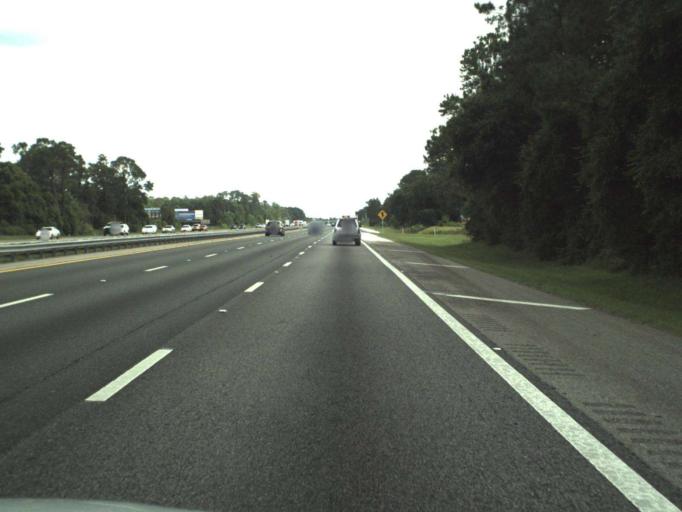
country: US
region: Florida
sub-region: Volusia County
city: Lake Helen
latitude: 28.9867
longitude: -81.2475
